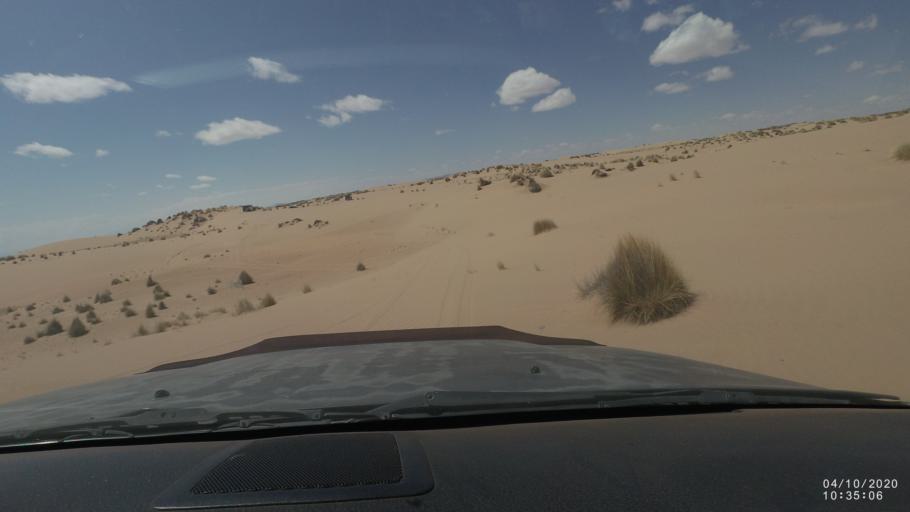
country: BO
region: Oruro
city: Poopo
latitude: -18.7049
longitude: -67.4760
